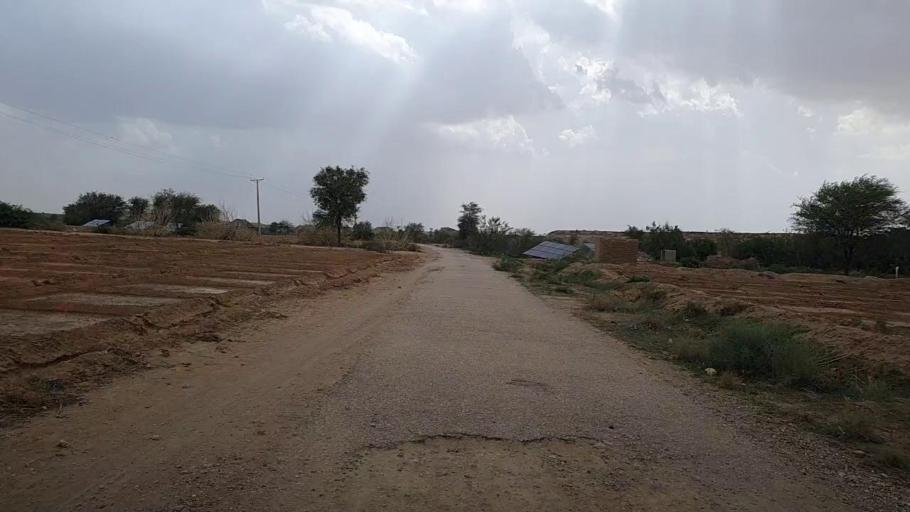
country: PK
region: Sindh
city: Jamshoro
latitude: 25.3954
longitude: 67.6944
